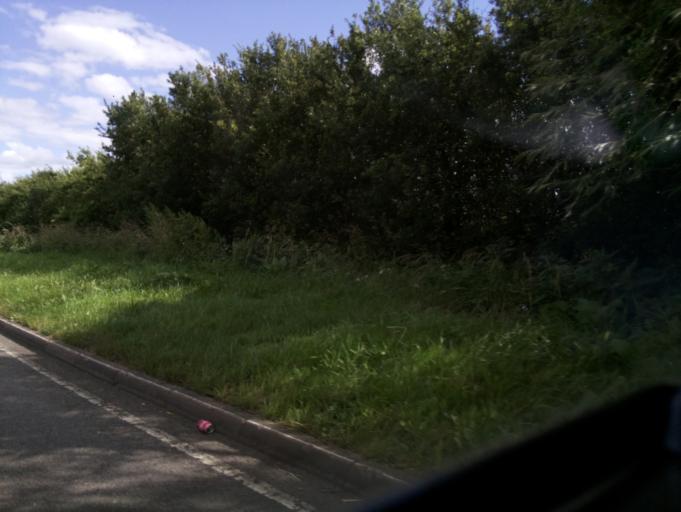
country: GB
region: England
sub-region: Leicestershire
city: Hathern
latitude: 52.8015
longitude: -1.2680
